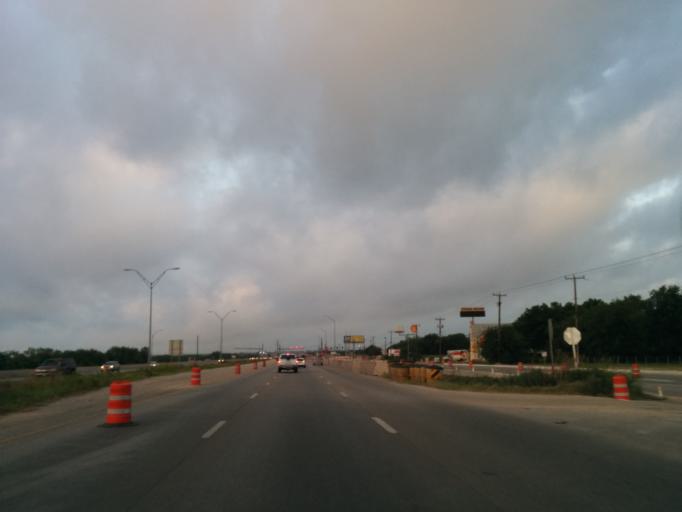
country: US
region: Texas
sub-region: Bexar County
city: Helotes
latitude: 29.5185
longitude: -98.6931
